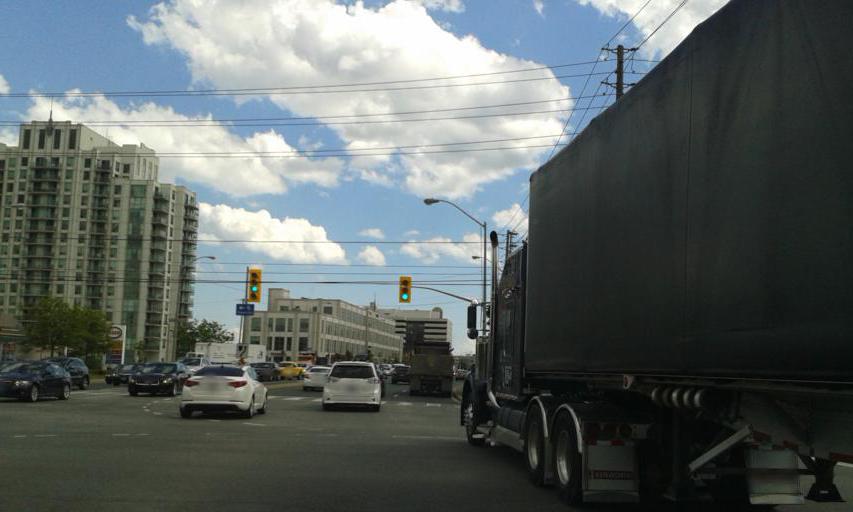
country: CA
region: Ontario
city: Scarborough
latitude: 43.7942
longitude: -79.2390
